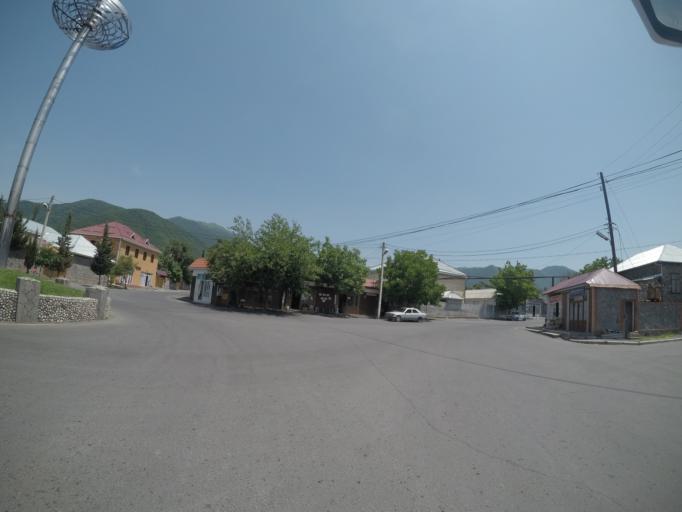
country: AZ
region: Qakh Rayon
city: Qax
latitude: 41.4161
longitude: 46.9201
